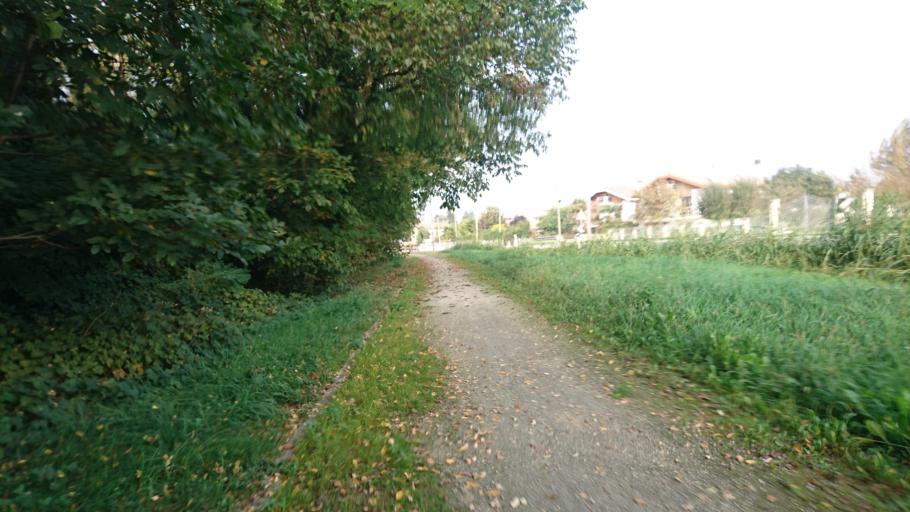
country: IT
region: Veneto
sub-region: Provincia di Padova
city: Curtarolo
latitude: 45.5194
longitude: 11.8446
